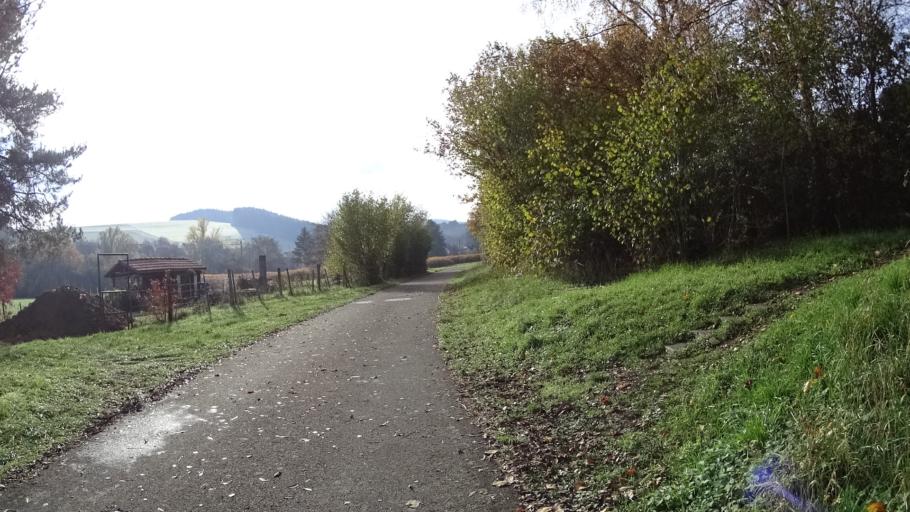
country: DE
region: Rheinland-Pfalz
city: Sankt Julian
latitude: 49.6144
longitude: 7.5319
